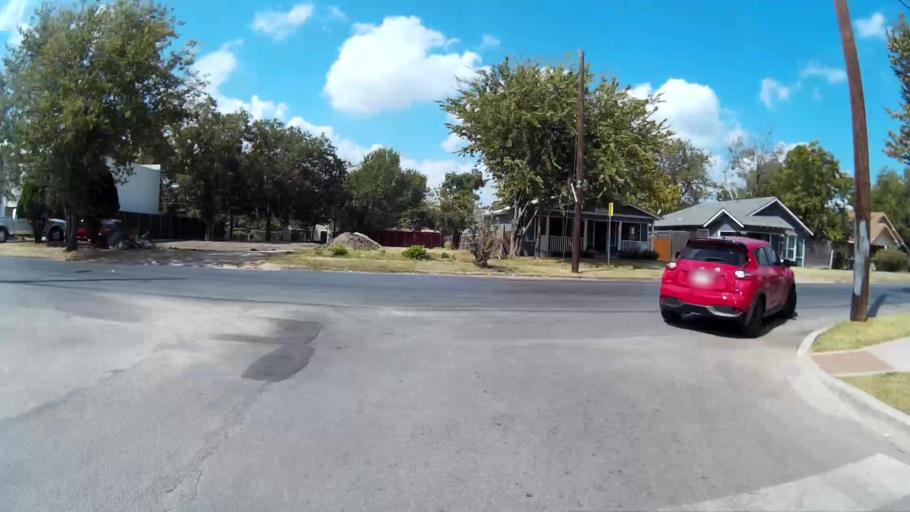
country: US
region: Texas
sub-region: Dallas County
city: Highland Park
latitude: 32.8147
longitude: -96.7744
